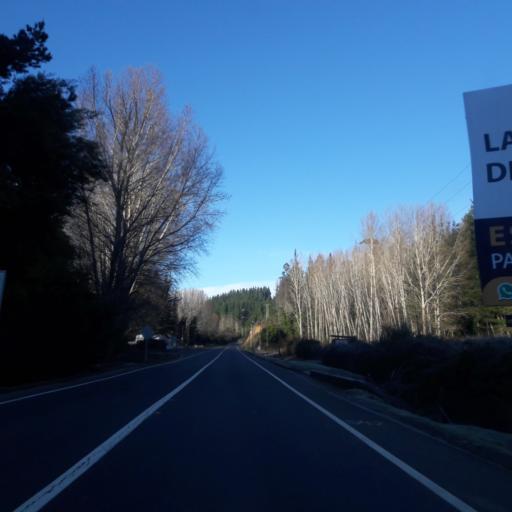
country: CL
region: Biobio
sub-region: Provincia de Concepcion
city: Lota
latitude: -37.2398
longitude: -72.9640
